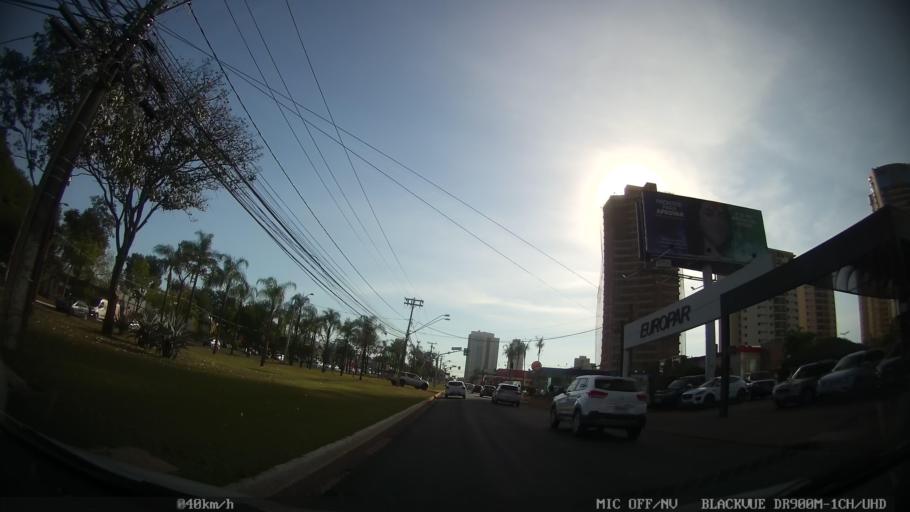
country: BR
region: Sao Paulo
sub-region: Ribeirao Preto
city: Ribeirao Preto
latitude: -21.2052
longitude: -47.8106
